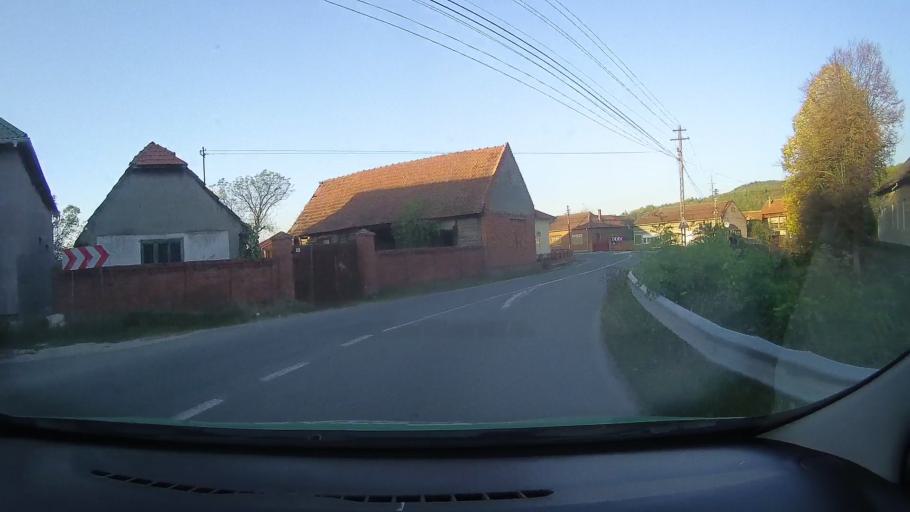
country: RO
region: Timis
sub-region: Comuna Traian Vuia
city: Traian Vuia
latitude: 45.7650
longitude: 22.0951
